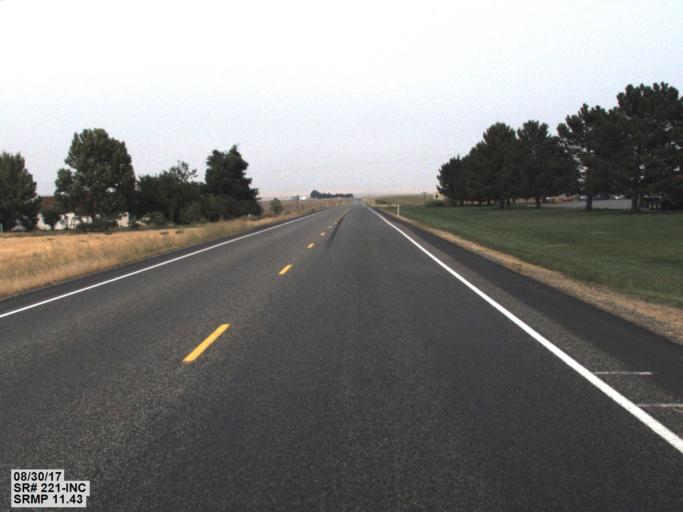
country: US
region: Washington
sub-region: Benton County
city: Prosser
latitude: 46.1007
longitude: -119.6018
